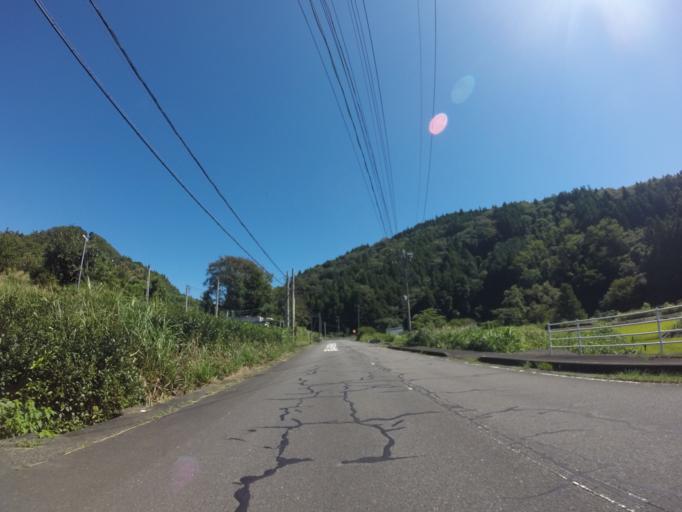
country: JP
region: Shizuoka
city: Kanaya
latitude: 34.9222
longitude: 138.1313
